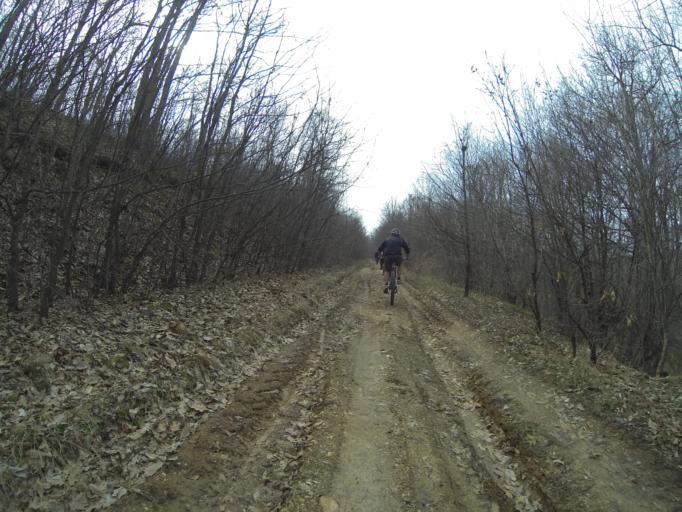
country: RO
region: Dolj
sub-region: Comuna Bucovat
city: Bucovat
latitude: 44.2794
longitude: 23.7067
